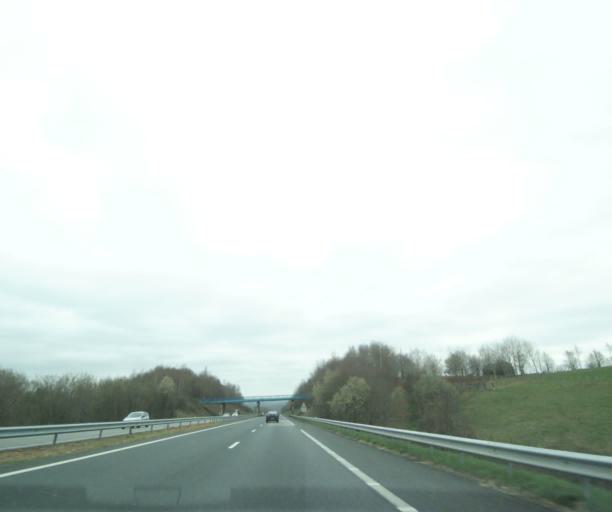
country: FR
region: Limousin
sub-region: Departement de la Correze
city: Uzerche
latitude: 45.4445
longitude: 1.5098
